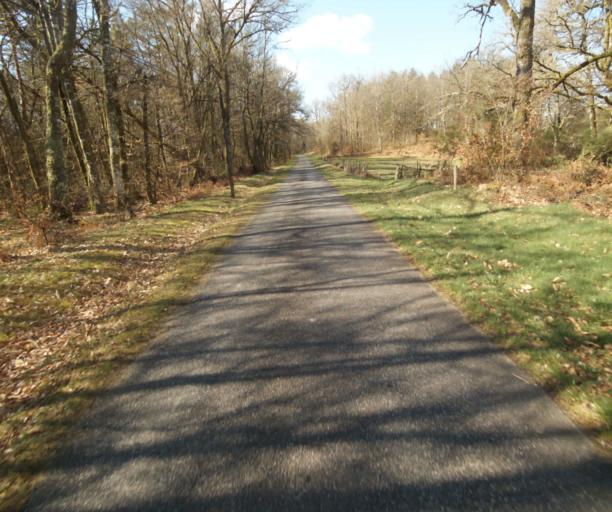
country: FR
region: Limousin
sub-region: Departement de la Correze
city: Laguenne
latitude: 45.2411
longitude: 1.9137
